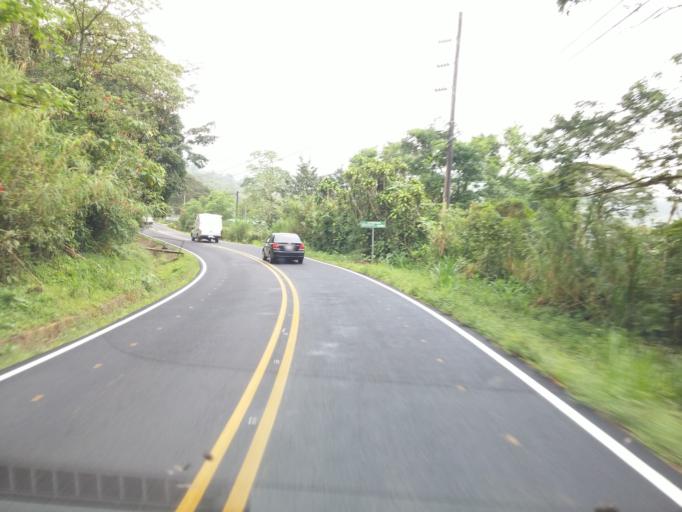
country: CR
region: Alajuela
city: San Ramon
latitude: 10.2125
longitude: -84.5388
